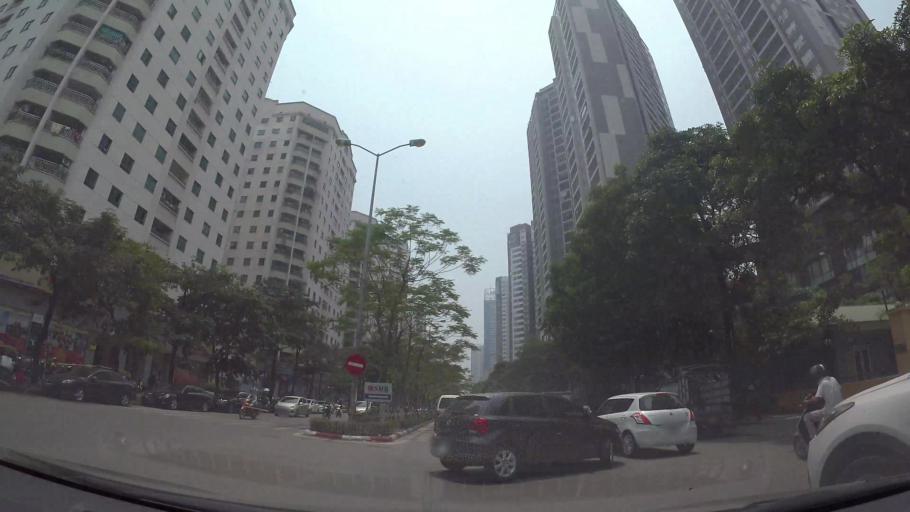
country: VN
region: Ha Noi
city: Thanh Xuan
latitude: 21.0096
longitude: 105.8003
